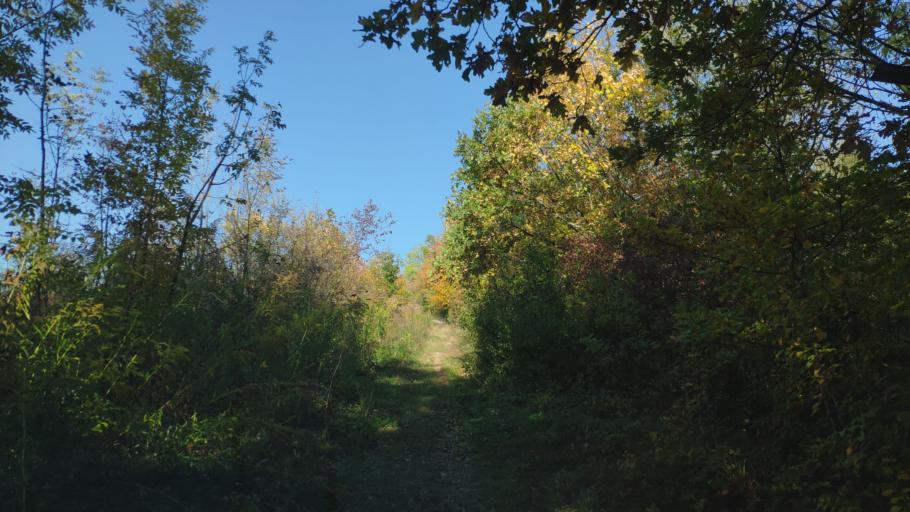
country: SK
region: Kosicky
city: Kosice
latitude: 48.7394
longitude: 21.2314
